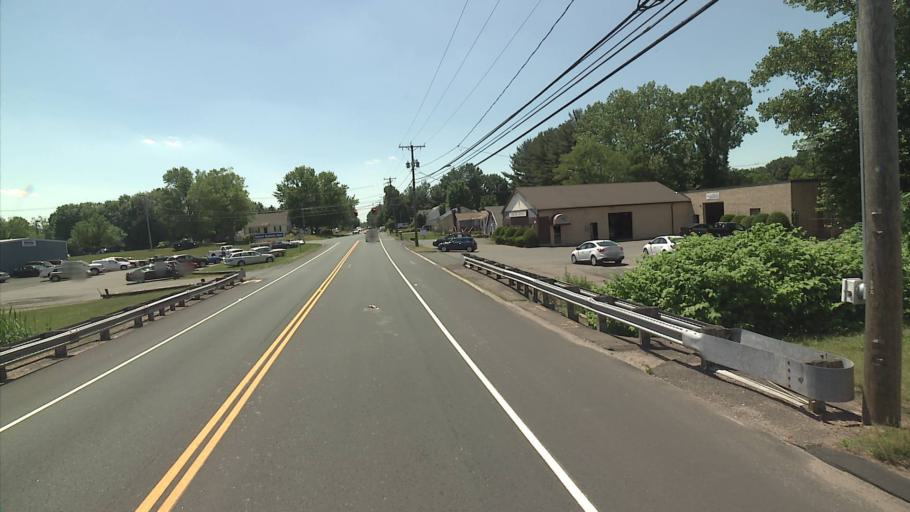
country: US
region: Connecticut
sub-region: Tolland County
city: Rockville
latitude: 41.8641
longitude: -72.4222
